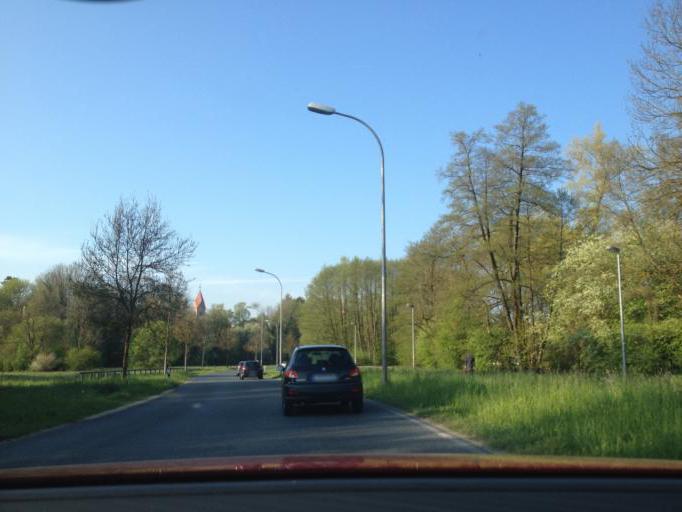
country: DE
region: Bavaria
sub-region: Regierungsbezirk Mittelfranken
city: Lauf an der Pegnitz
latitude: 49.5111
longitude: 11.2846
